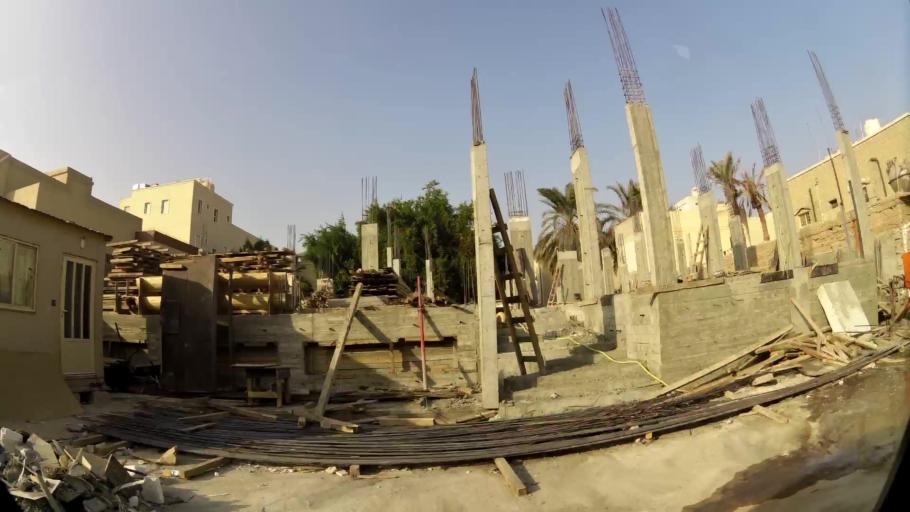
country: KW
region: Muhafazat Hawalli
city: Ar Rumaythiyah
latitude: 29.3193
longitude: 48.0812
